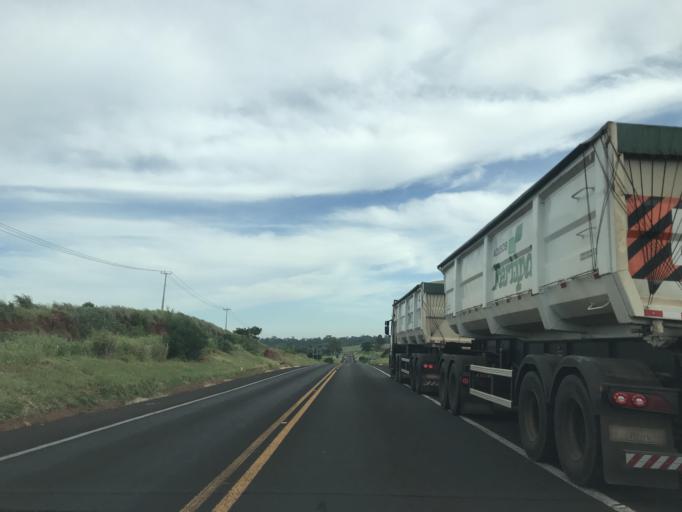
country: BR
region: Parana
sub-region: Paranavai
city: Paranavai
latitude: -23.0342
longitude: -52.4795
